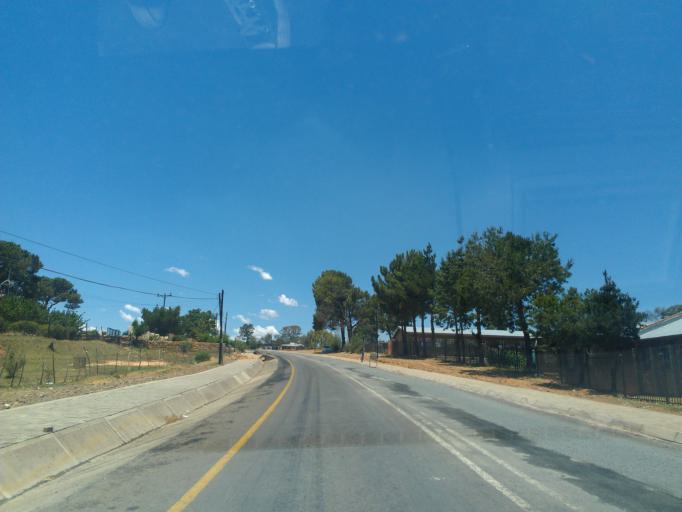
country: LS
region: Berea
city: Teyateyaneng
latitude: -29.1133
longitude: 27.9679
